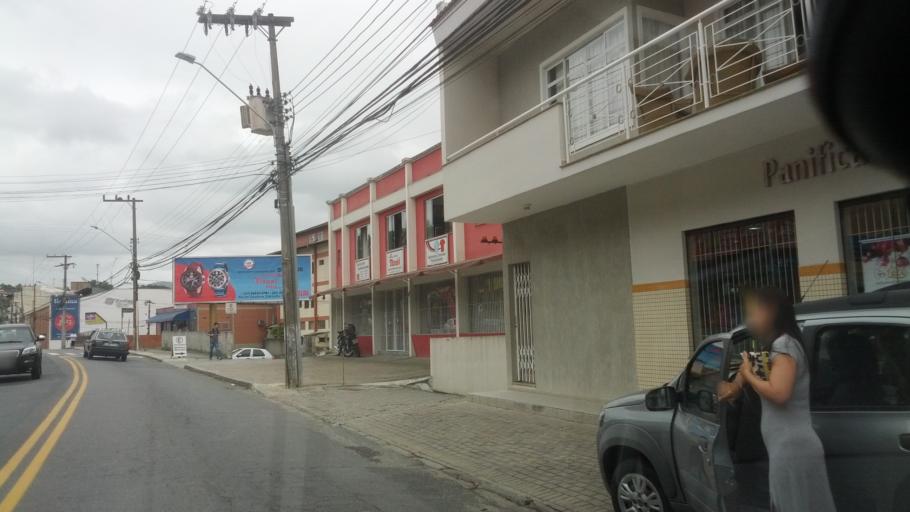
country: BR
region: Santa Catarina
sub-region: Blumenau
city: Blumenau
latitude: -26.9112
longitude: -49.0951
